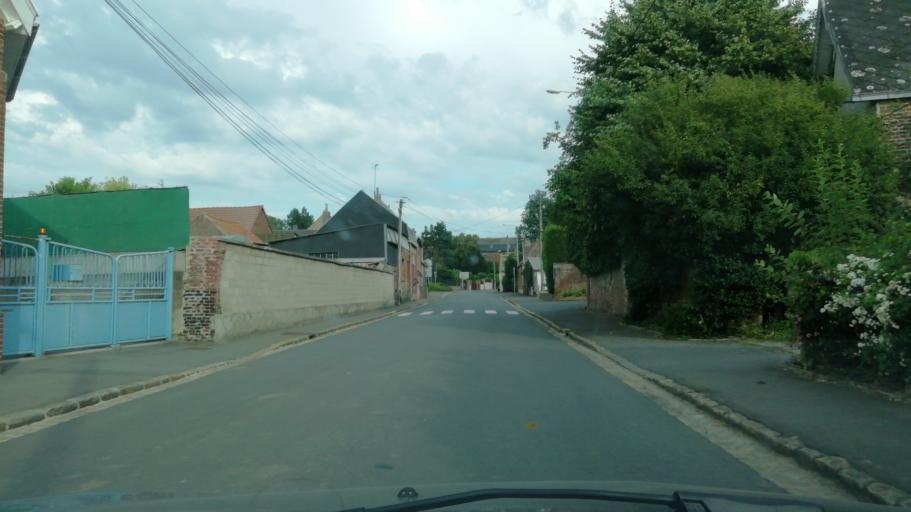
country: FR
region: Nord-Pas-de-Calais
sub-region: Departement du Nord
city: Rieux-en-Cambresis
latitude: 50.1666
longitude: 3.3451
